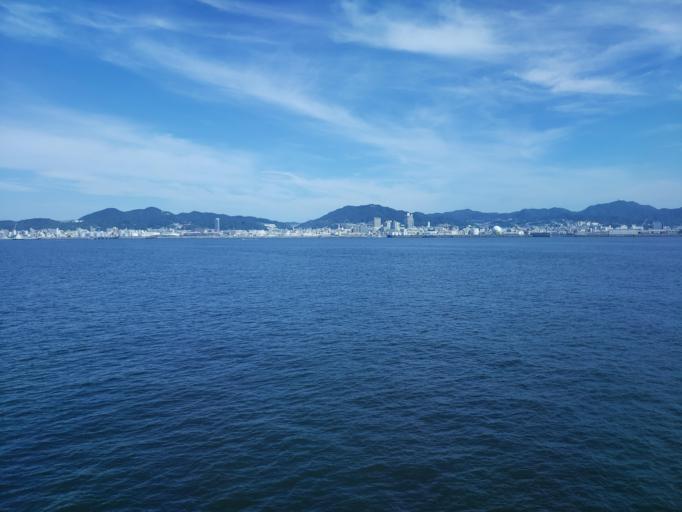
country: JP
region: Hyogo
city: Kobe
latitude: 34.6311
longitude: 135.1599
